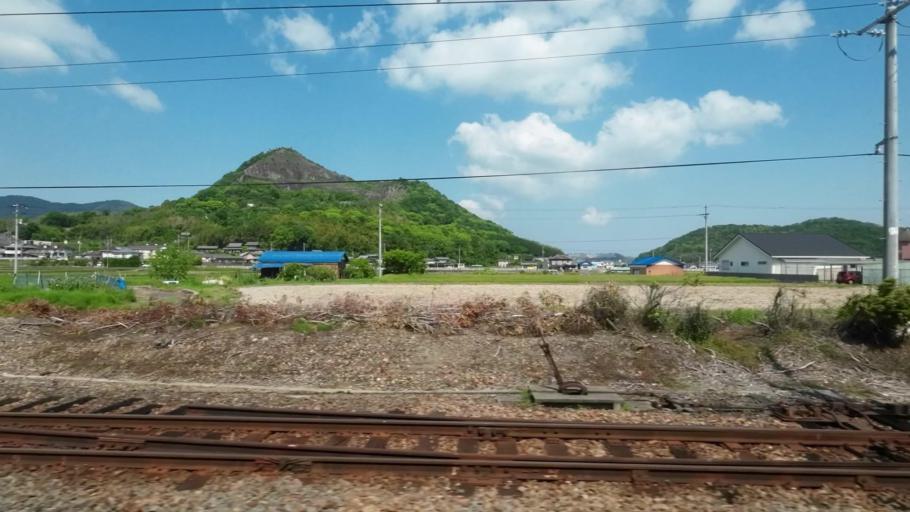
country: JP
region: Kagawa
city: Kan'onjicho
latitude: 34.1847
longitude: 133.7117
